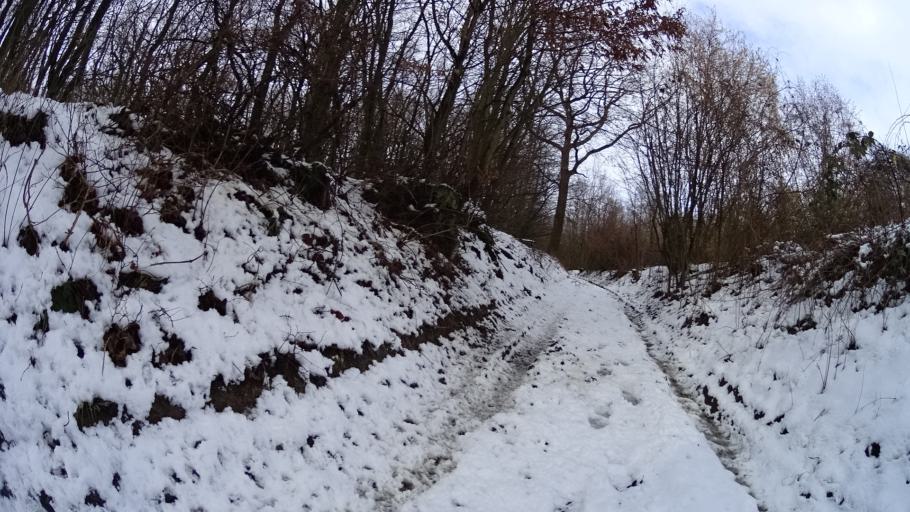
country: AT
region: Lower Austria
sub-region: Politischer Bezirk Korneuburg
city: Niederhollabrunn
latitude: 48.4135
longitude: 16.3022
